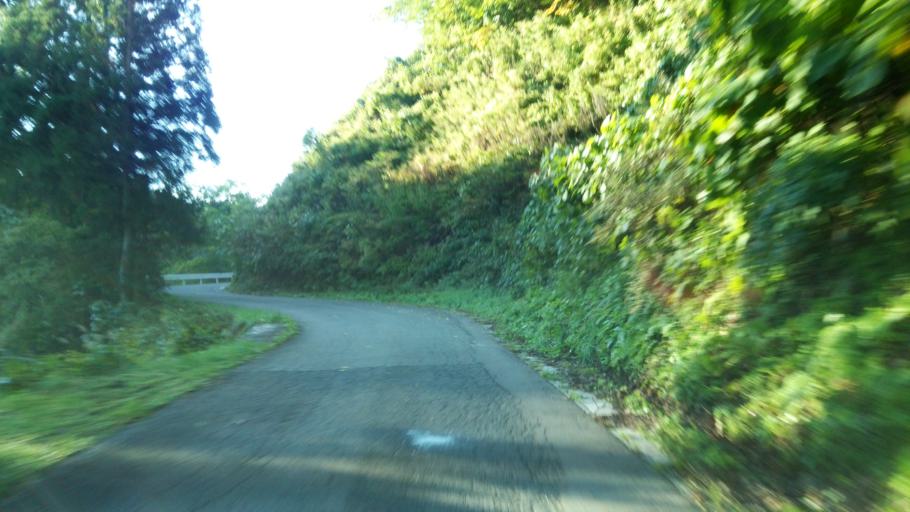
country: JP
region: Fukushima
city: Kitakata
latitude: 37.3973
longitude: 139.7358
